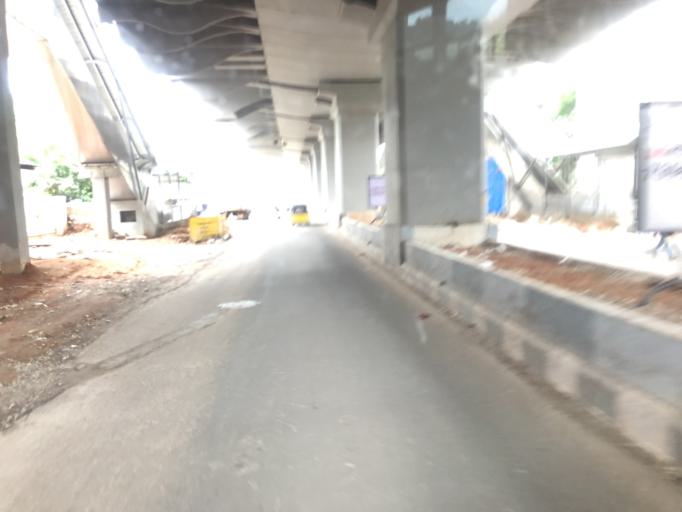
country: IN
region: Telangana
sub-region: Rangareddi
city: Kukatpalli
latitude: 17.4299
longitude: 78.4236
